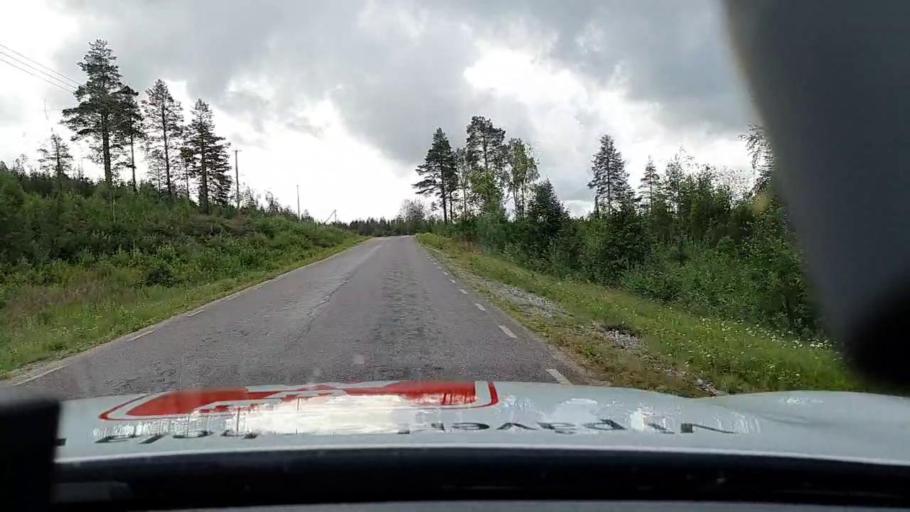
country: SE
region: Norrbotten
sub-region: Overkalix Kommun
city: OEverkalix
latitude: 66.2589
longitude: 23.1105
